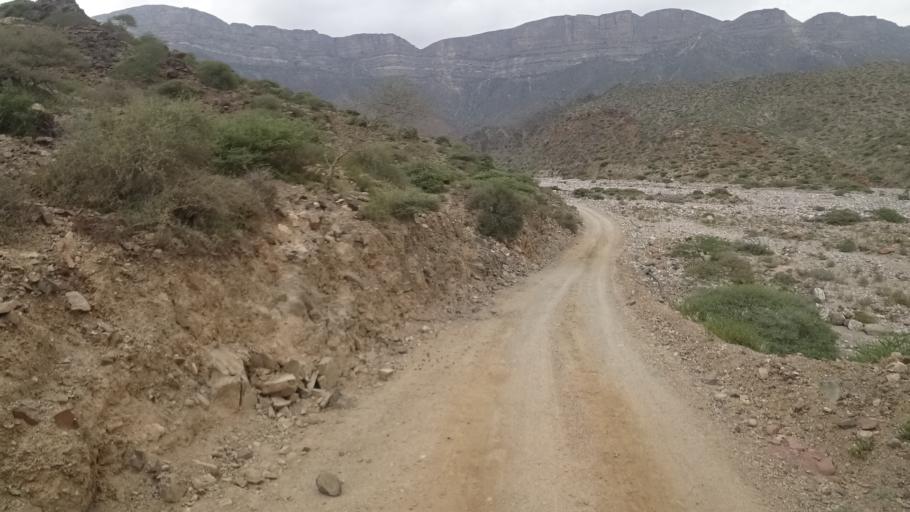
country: OM
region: Zufar
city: Salalah
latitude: 17.1755
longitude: 54.9503
